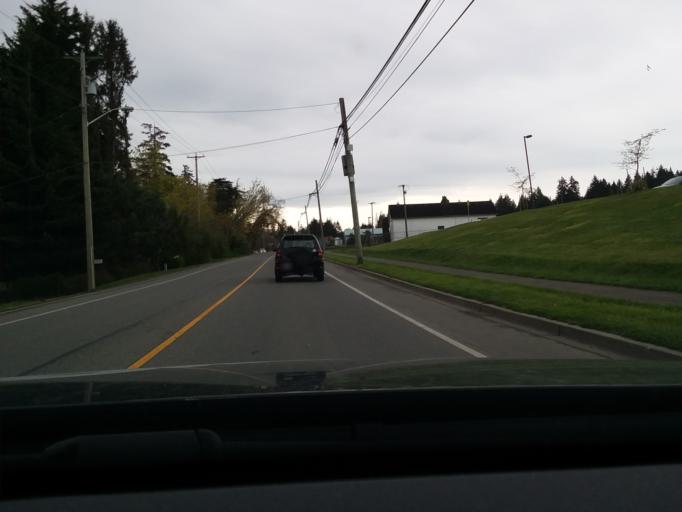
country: CA
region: British Columbia
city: North Saanich
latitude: 48.6238
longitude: -123.4184
